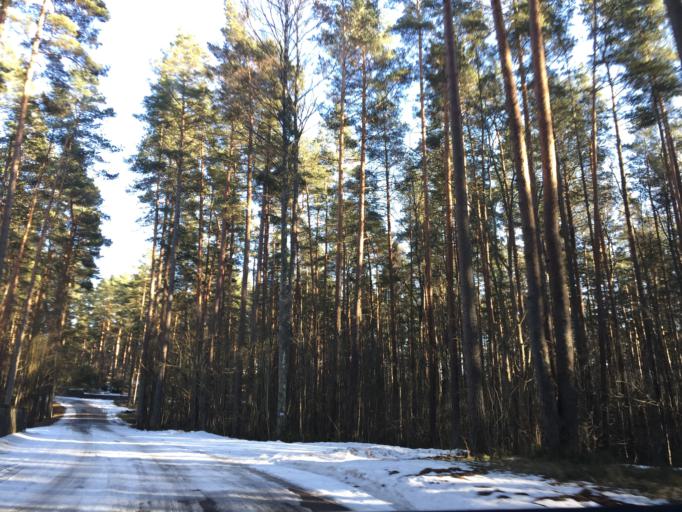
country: LV
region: Babite
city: Pinki
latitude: 56.9305
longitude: 23.9095
